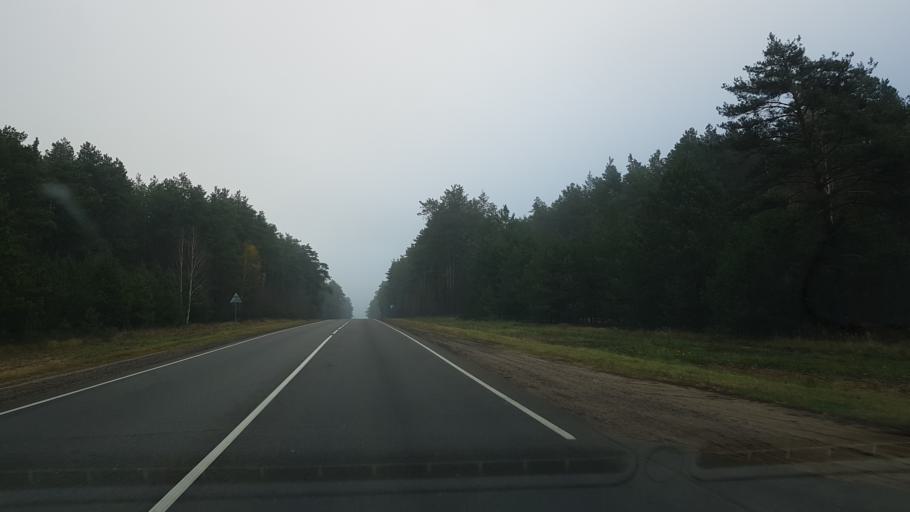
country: BY
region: Mogilev
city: Babruysk
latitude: 53.1618
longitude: 29.3243
